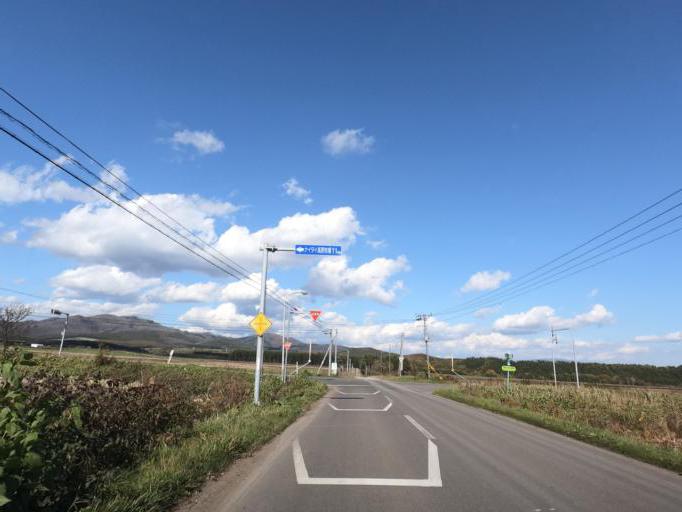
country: JP
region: Hokkaido
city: Otofuke
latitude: 43.2569
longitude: 143.2542
